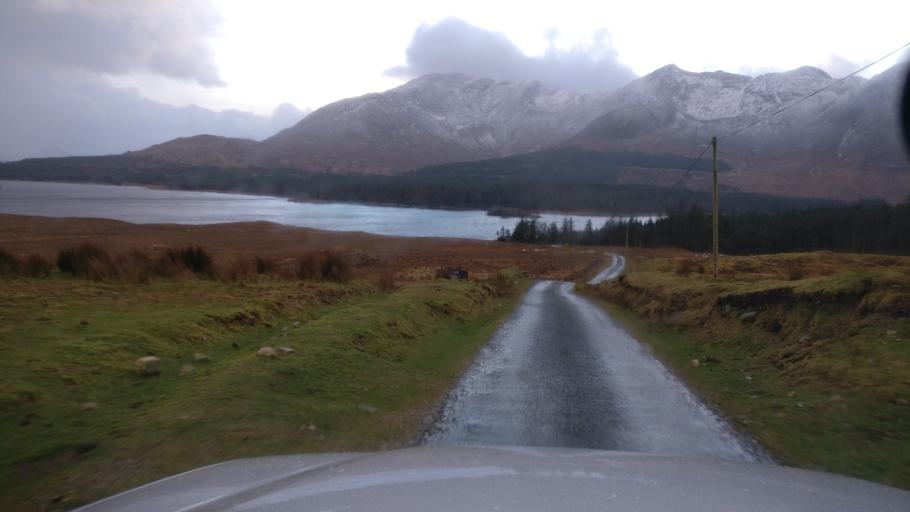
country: IE
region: Connaught
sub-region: County Galway
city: Clifden
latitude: 53.5185
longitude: -9.7327
